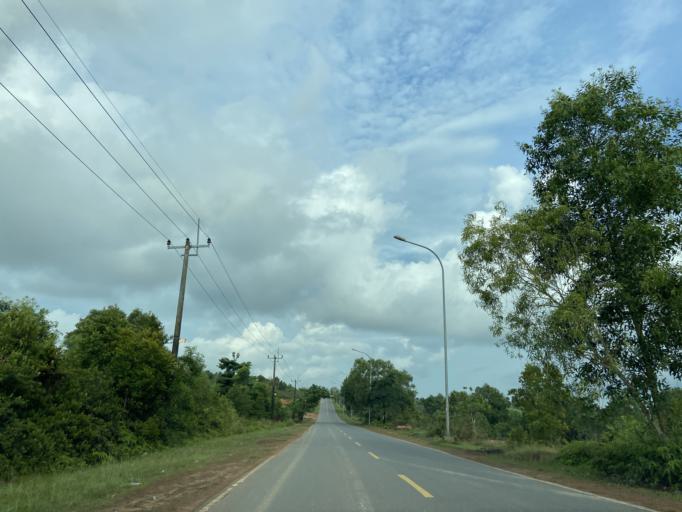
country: ID
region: Riau Islands
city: Tanjungpinang
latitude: 0.9380
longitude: 104.0909
